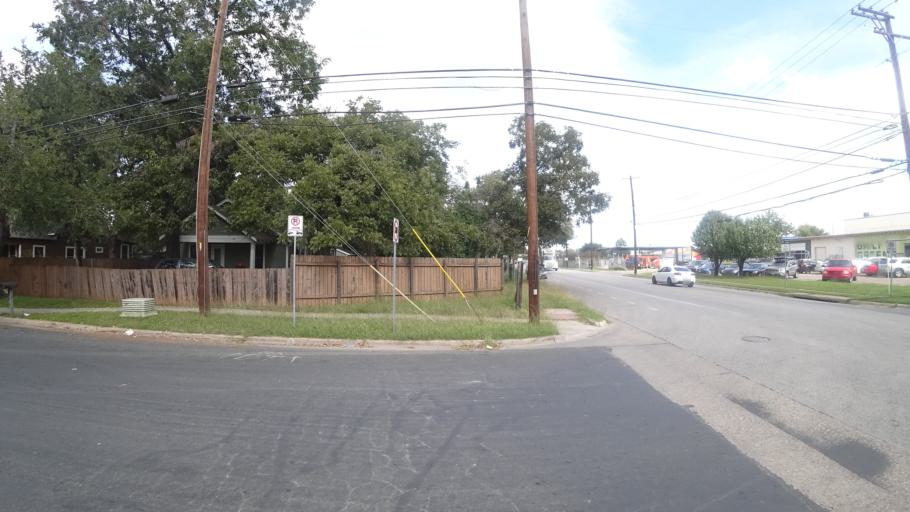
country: US
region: Texas
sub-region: Travis County
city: Austin
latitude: 30.2640
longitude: -97.6967
